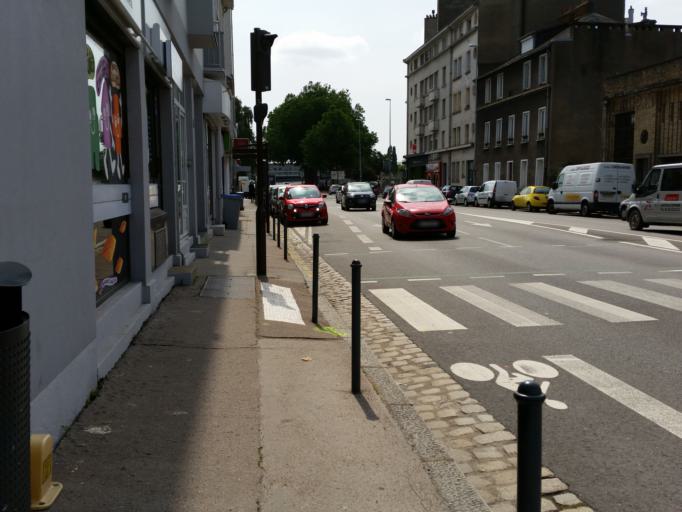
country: FR
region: Pays de la Loire
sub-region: Departement de la Loire-Atlantique
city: Nantes
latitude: 47.2014
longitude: -1.5465
